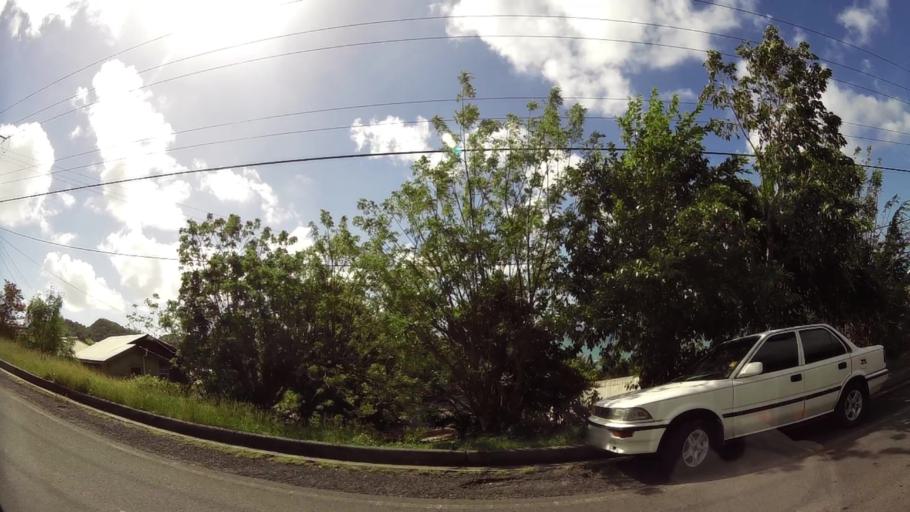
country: LC
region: Laborie Quarter
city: Laborie
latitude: 13.7534
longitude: -60.9946
